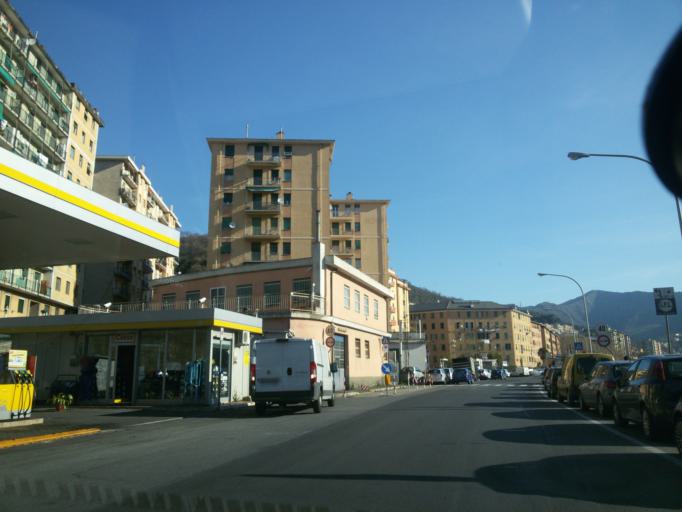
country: IT
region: Liguria
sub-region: Provincia di Genova
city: Piccarello
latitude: 44.4419
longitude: 8.9638
